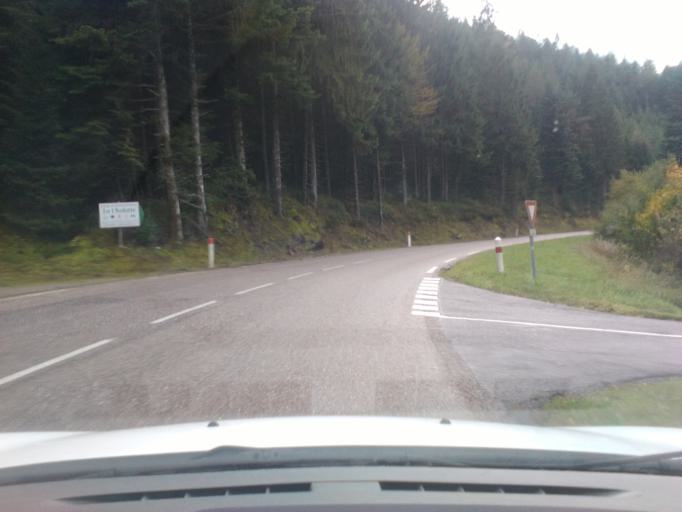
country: FR
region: Lorraine
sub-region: Departement des Vosges
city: Taintrux
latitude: 48.2716
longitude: 6.8346
